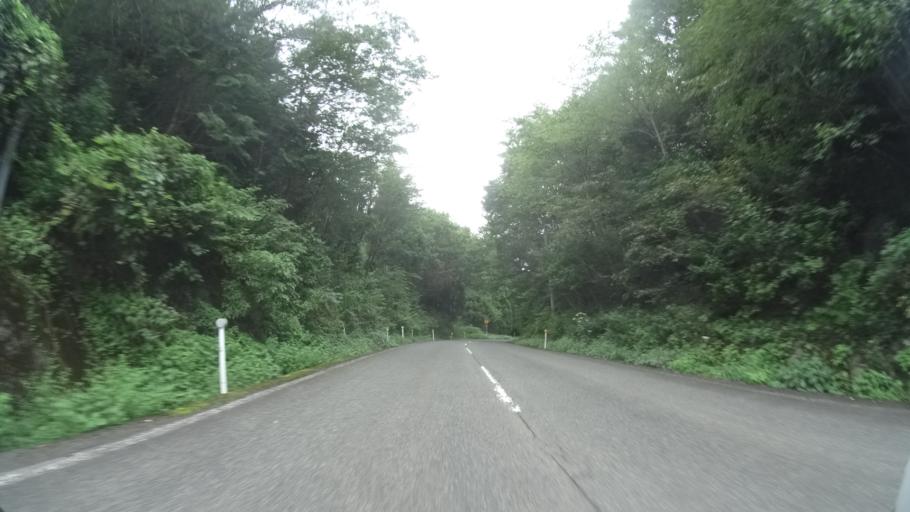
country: JP
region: Tottori
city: Kurayoshi
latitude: 35.4046
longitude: 133.9974
